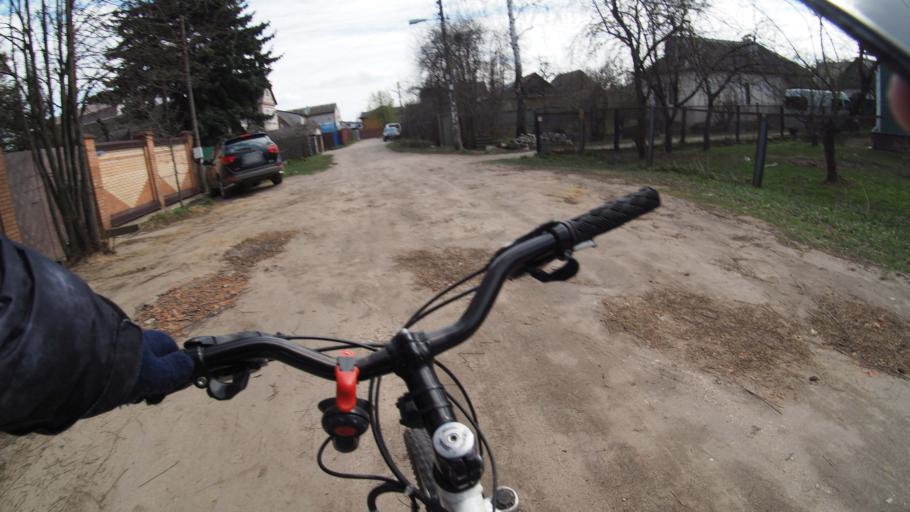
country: RU
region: Moskovskaya
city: Ramenskoye
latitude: 55.5605
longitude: 38.2213
